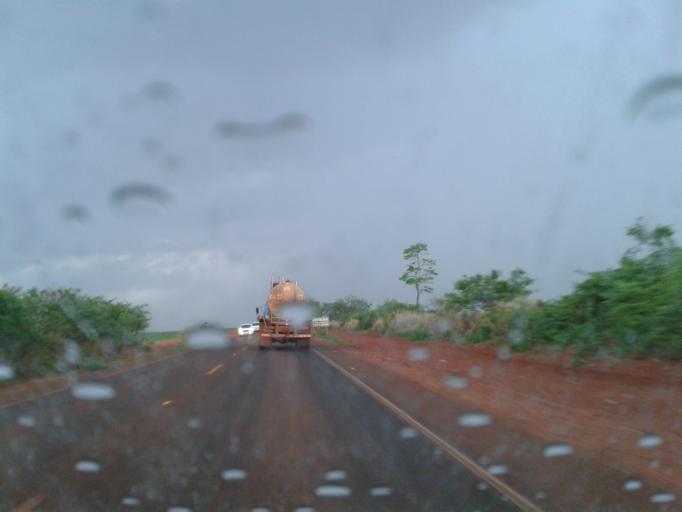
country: BR
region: Goias
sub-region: Quirinopolis
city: Quirinopolis
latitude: -18.5768
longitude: -50.4381
